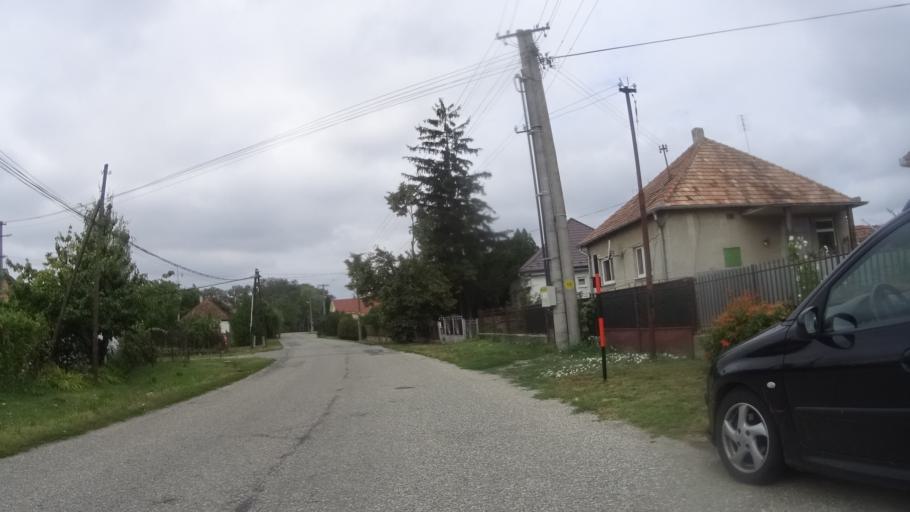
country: HU
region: Komarom-Esztergom
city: Acs
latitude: 47.7686
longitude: 17.9793
